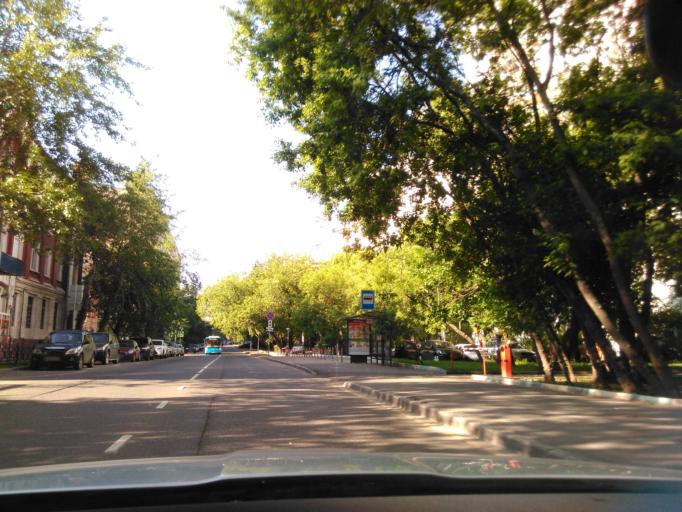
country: RU
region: Moskovskaya
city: Dorogomilovo
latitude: 55.7715
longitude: 37.5728
